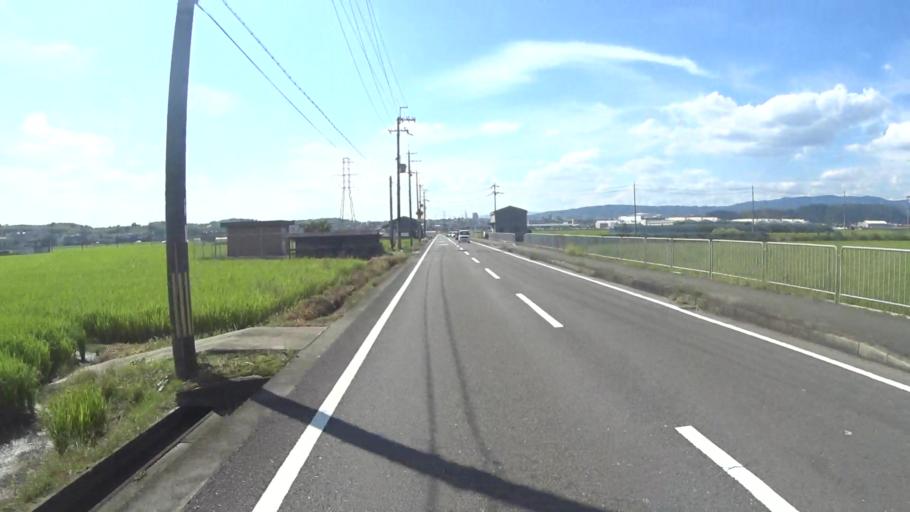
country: JP
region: Kyoto
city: Yawata
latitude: 34.8580
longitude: 135.7270
